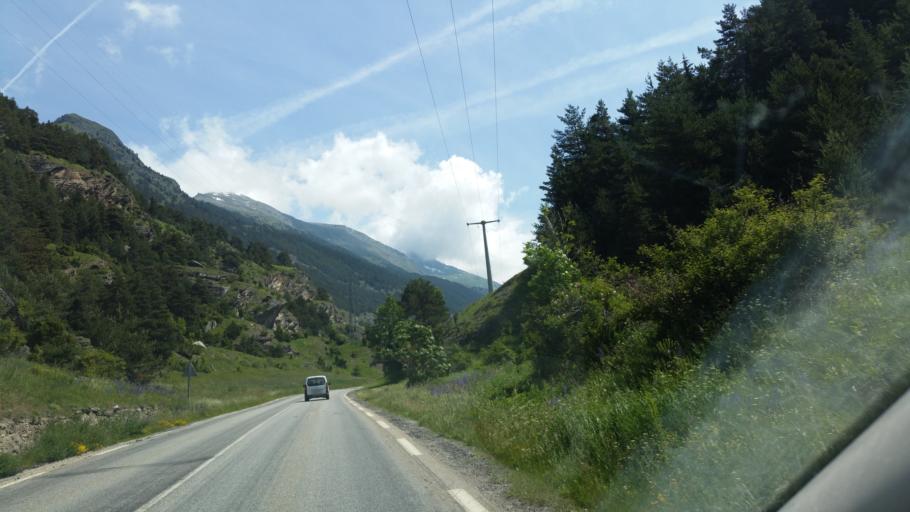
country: FR
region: Rhone-Alpes
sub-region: Departement de la Savoie
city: Modane
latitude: 45.2798
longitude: 6.8211
